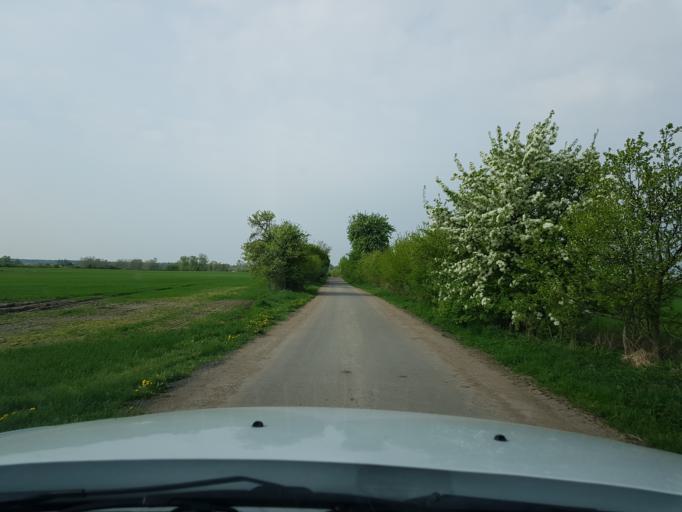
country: PL
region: West Pomeranian Voivodeship
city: Trzcinsko Zdroj
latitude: 52.9579
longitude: 14.5888
